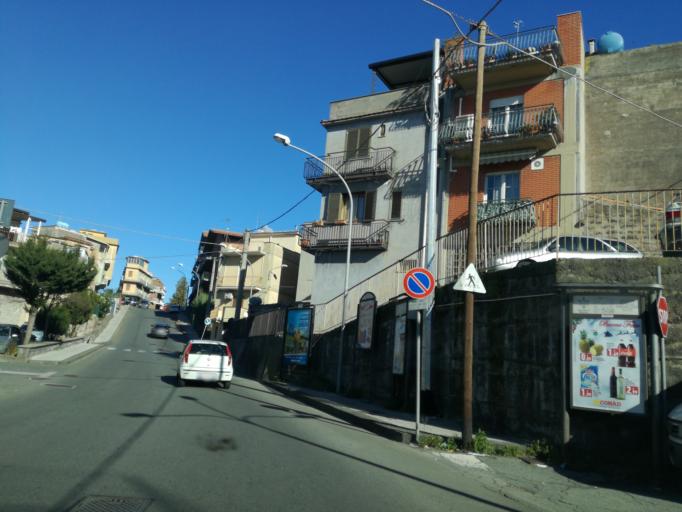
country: IT
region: Sicily
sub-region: Catania
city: Bronte
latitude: 37.7855
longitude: 14.8378
